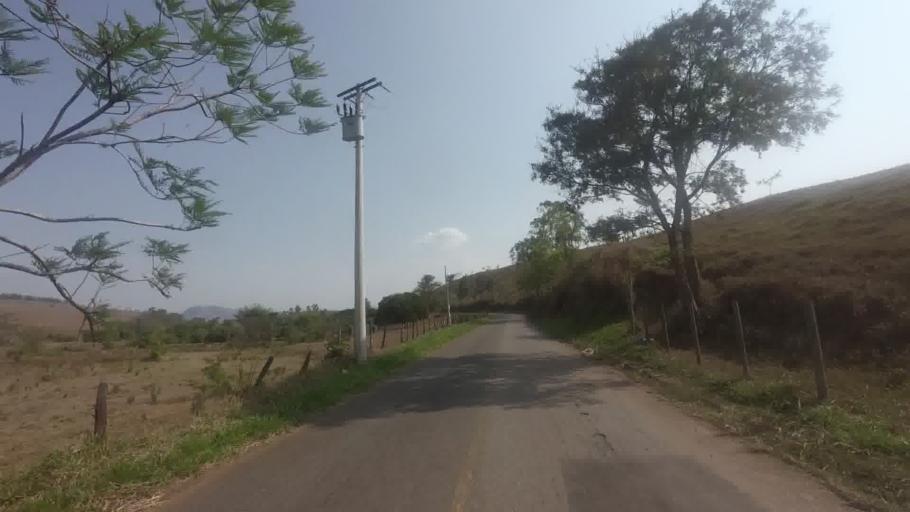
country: BR
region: Rio de Janeiro
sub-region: Bom Jesus Do Itabapoana
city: Bom Jesus do Itabapoana
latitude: -21.1382
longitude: -41.5679
